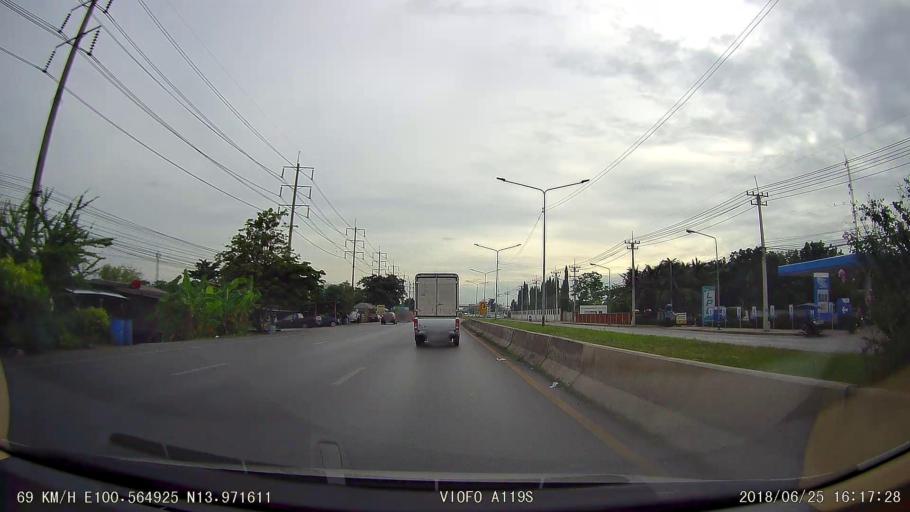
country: TH
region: Phra Nakhon Si Ayutthaya
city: Ban Bang Kadi Pathum Thani
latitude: 13.9716
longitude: 100.5649
